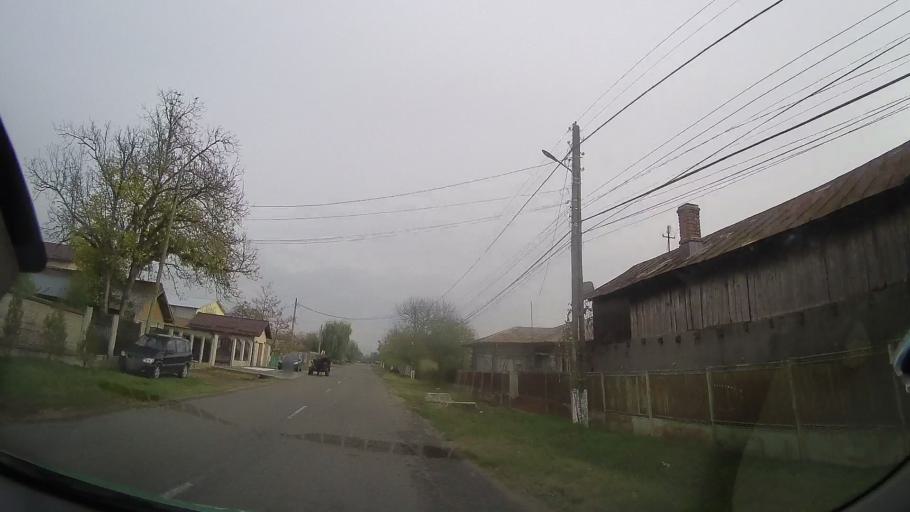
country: RO
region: Prahova
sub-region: Comuna Balta Doamnei
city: Balta Doamnei
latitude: 44.7603
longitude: 26.1605
